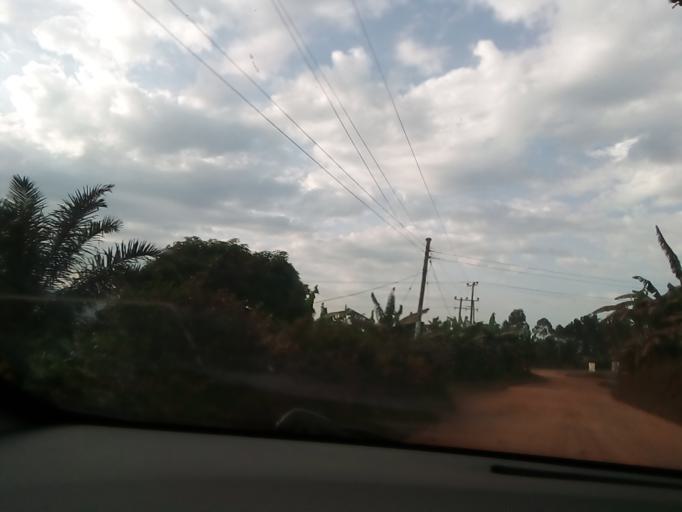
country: UG
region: Central Region
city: Masaka
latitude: -0.3543
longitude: 31.7215
